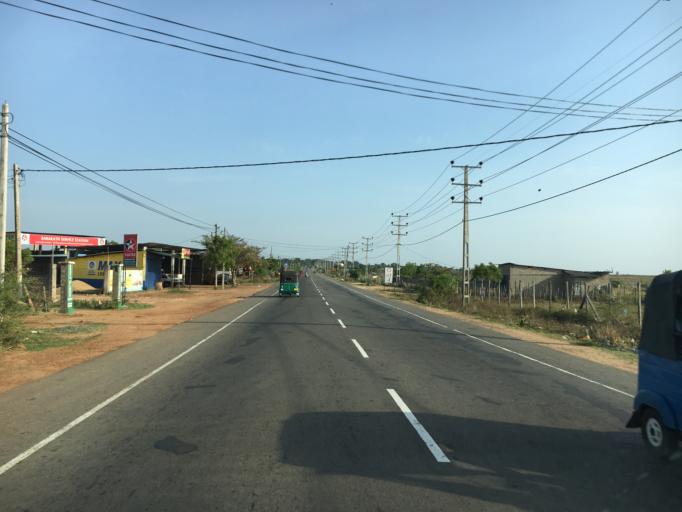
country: LK
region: Eastern Province
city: Eravur Town
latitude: 7.9336
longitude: 81.5109
